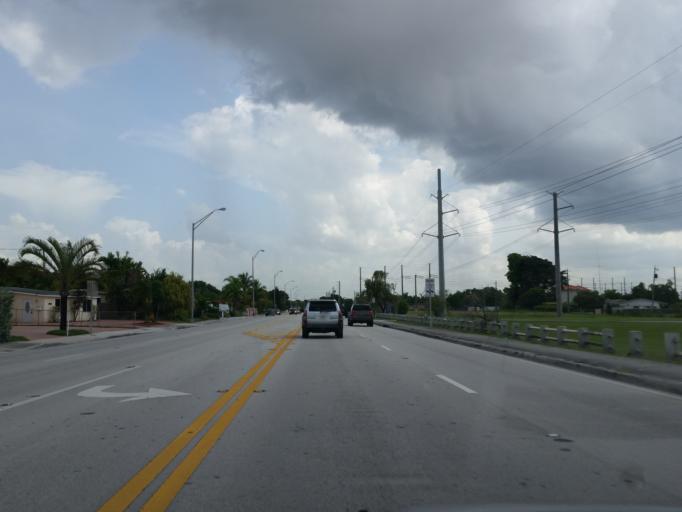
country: US
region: Florida
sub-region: Miami-Dade County
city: Westwood Lake
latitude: 25.7275
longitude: -80.3675
